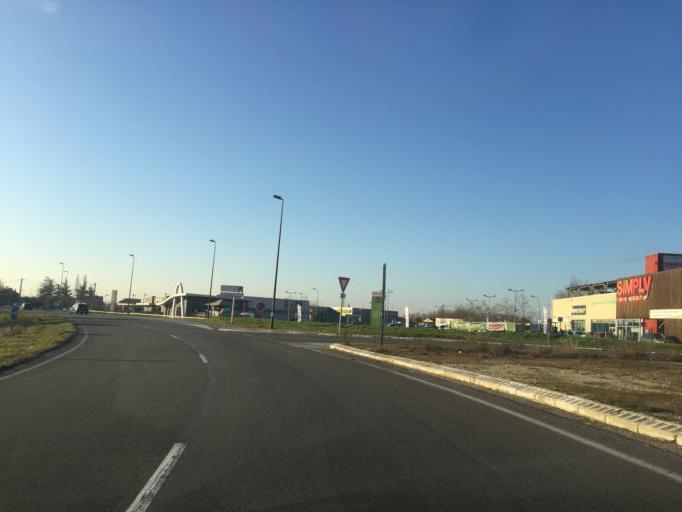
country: FR
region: Provence-Alpes-Cote d'Azur
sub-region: Departement du Vaucluse
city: Le Pontet
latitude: 43.9507
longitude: 4.8602
